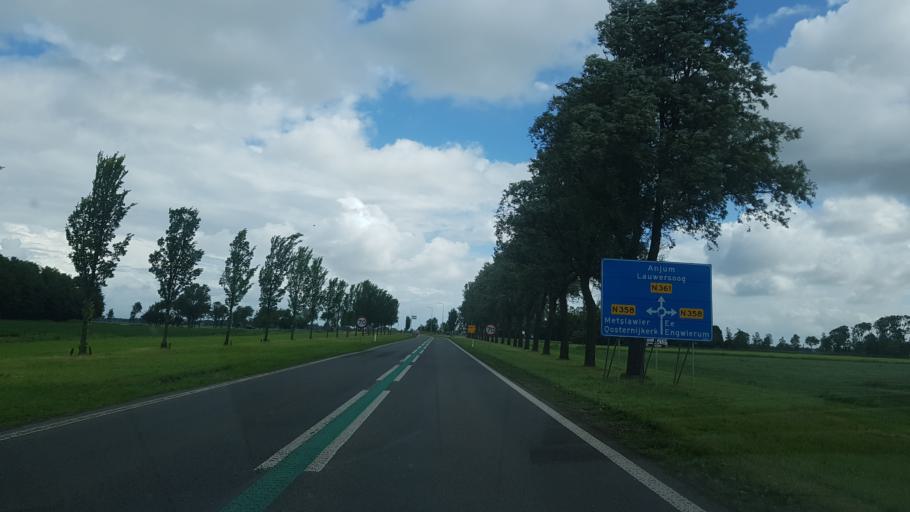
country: NL
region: Friesland
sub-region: Gemeente Dongeradeel
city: Anjum
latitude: 53.3560
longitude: 6.0726
